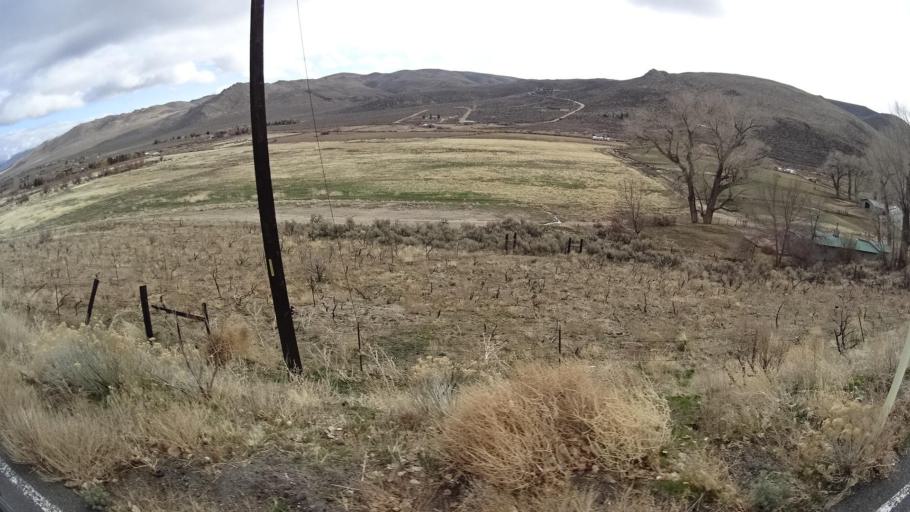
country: US
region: Nevada
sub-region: Washoe County
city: Cold Springs
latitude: 39.8402
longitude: -119.9356
